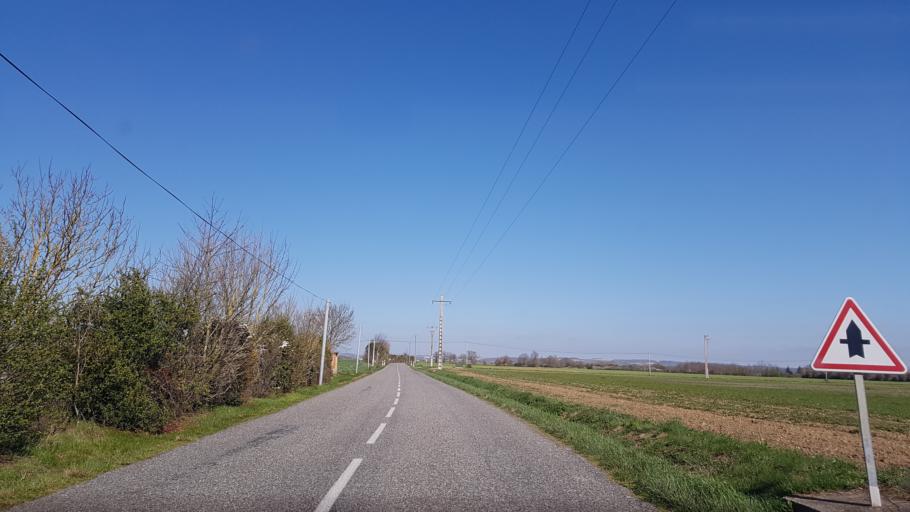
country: FR
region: Languedoc-Roussillon
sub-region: Departement de l'Aude
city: Belpech
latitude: 43.1581
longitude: 1.7087
